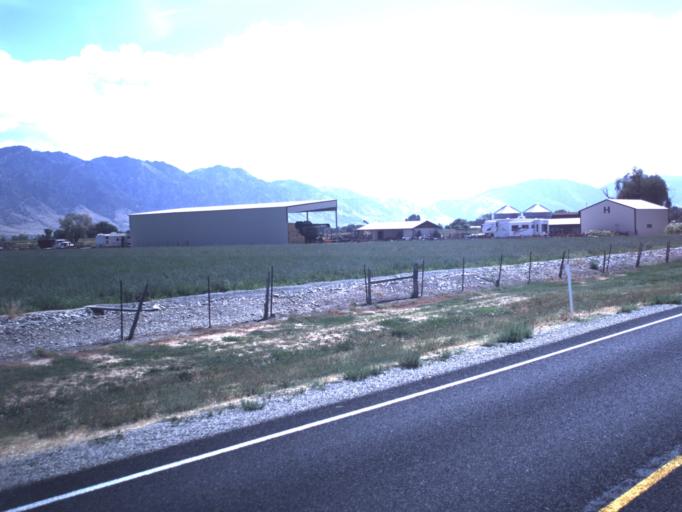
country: US
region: Utah
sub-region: Box Elder County
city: Honeyville
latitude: 41.6328
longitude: -112.1278
